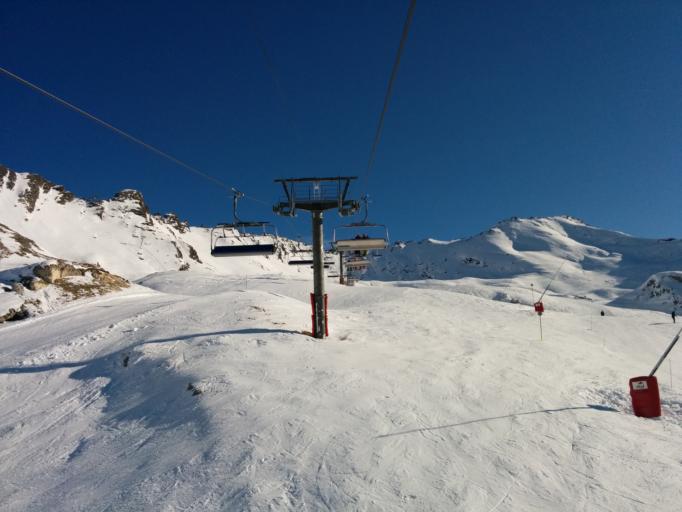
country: FR
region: Rhone-Alpes
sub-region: Departement de la Savoie
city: Val-d'Isere
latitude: 45.4246
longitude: 7.0066
